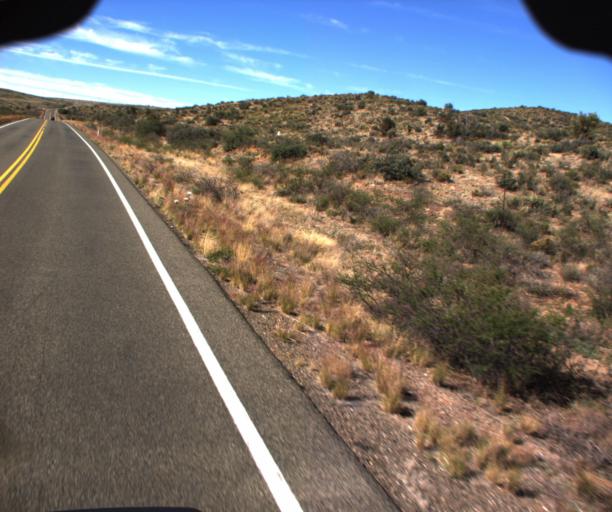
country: US
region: Arizona
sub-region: Yavapai County
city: Congress
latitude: 34.3493
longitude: -112.6823
